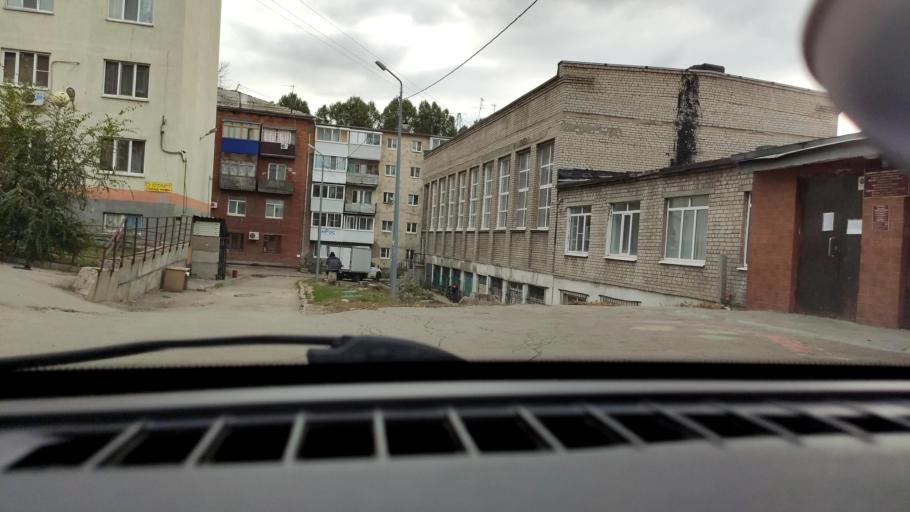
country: RU
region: Samara
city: Samara
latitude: 53.1717
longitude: 50.1899
